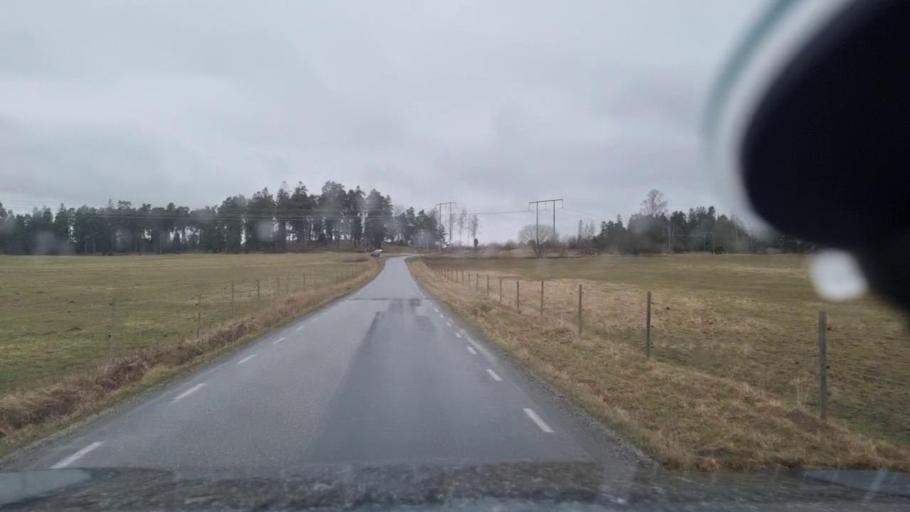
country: SE
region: Stockholm
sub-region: Vallentuna Kommun
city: Vallentuna
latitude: 59.5270
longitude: 18.0399
